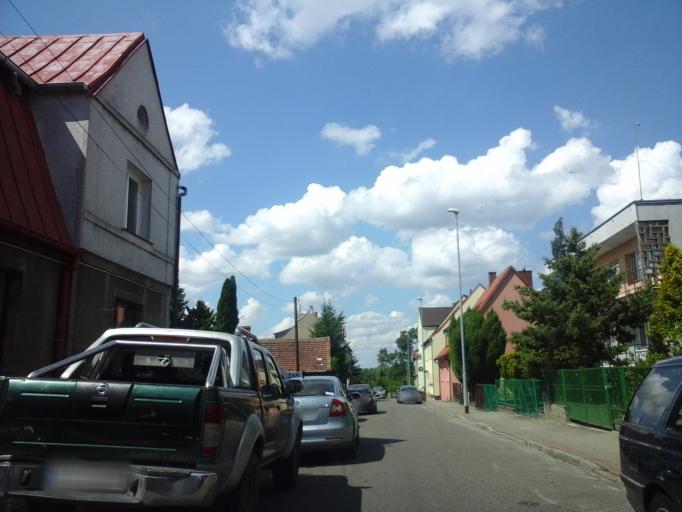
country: PL
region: West Pomeranian Voivodeship
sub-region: Powiat choszczenski
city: Choszczno
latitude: 53.1685
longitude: 15.4059
